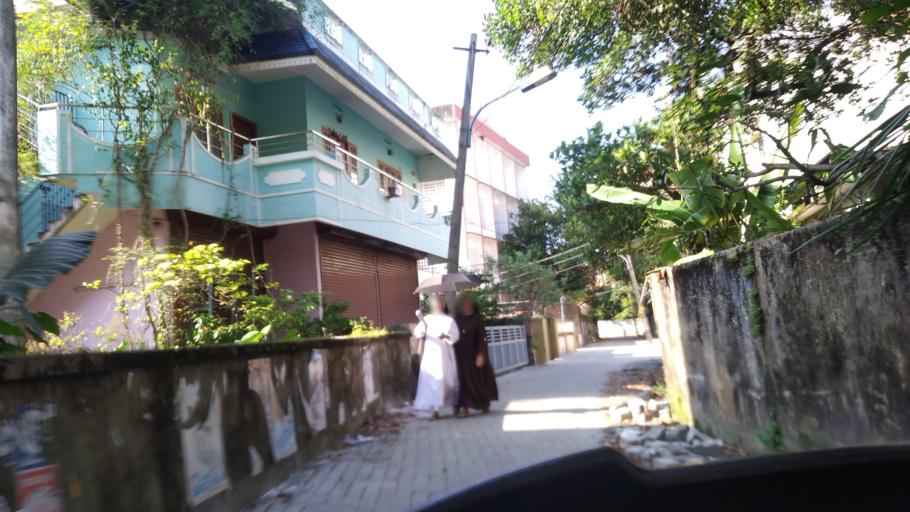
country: IN
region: Kerala
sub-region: Ernakulam
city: Cochin
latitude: 9.9835
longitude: 76.2802
